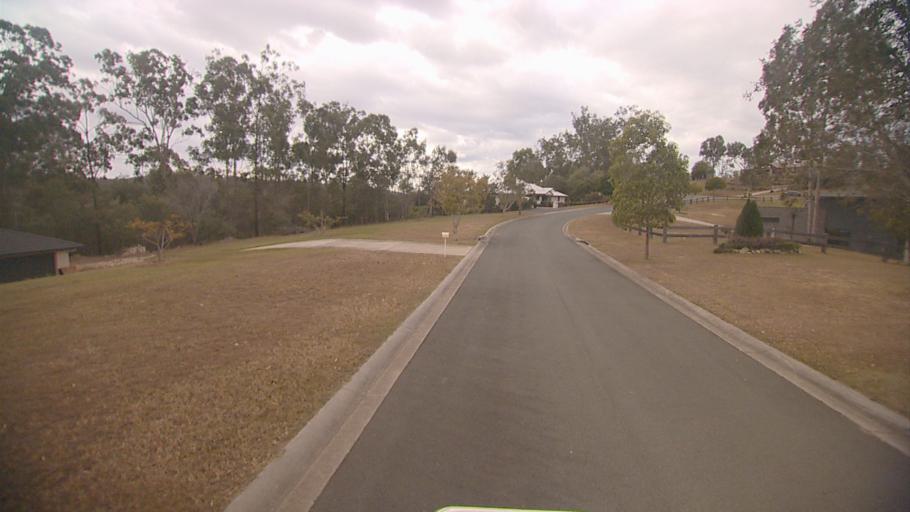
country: AU
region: Queensland
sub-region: Logan
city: Cedar Vale
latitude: -27.8684
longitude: 153.0722
